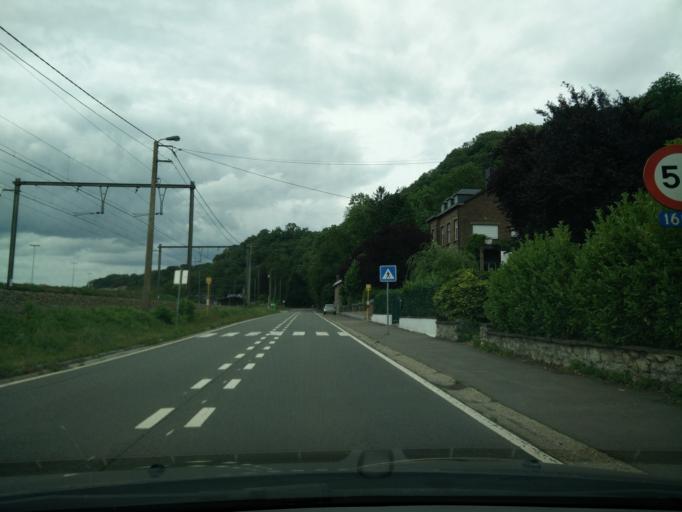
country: BE
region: Wallonia
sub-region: Province de Liege
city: Vise
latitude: 50.7172
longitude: 5.6908
